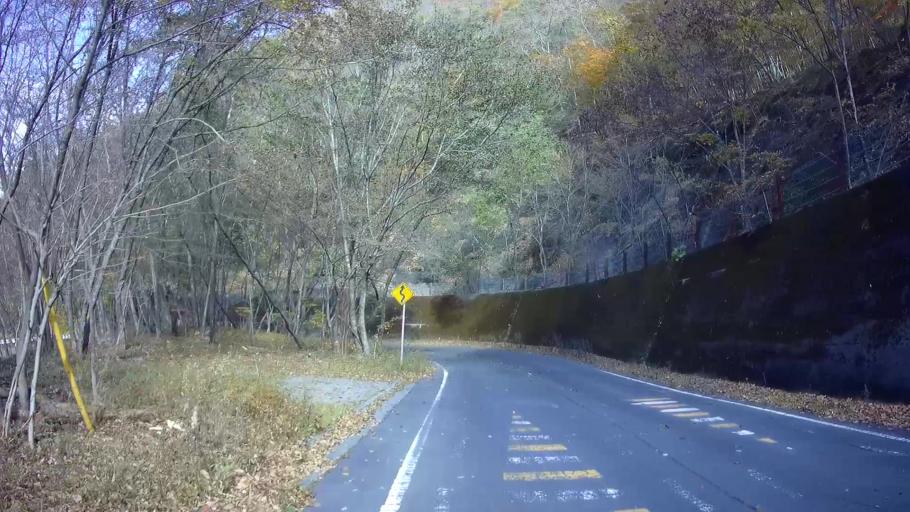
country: JP
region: Gunma
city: Nakanojomachi
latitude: 36.5259
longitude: 138.6605
